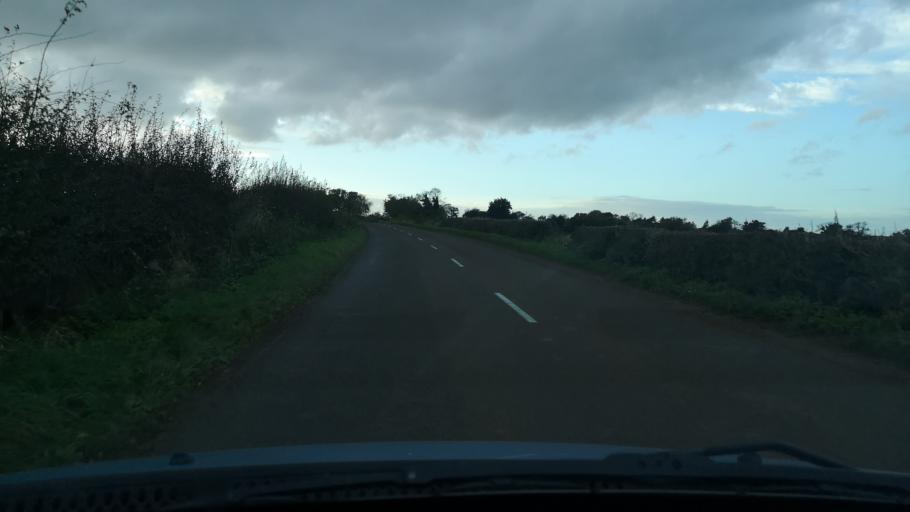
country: GB
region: England
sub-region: Doncaster
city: Norton
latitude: 53.6390
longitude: -1.2123
